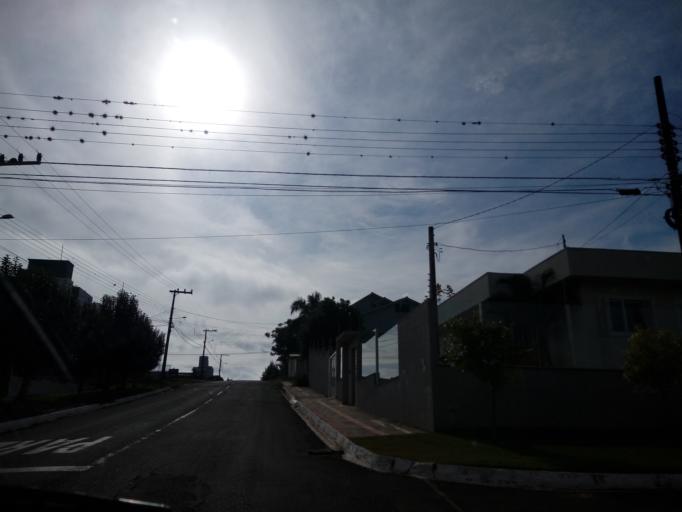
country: BR
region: Santa Catarina
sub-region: Chapeco
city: Chapeco
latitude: -27.0987
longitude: -52.6370
